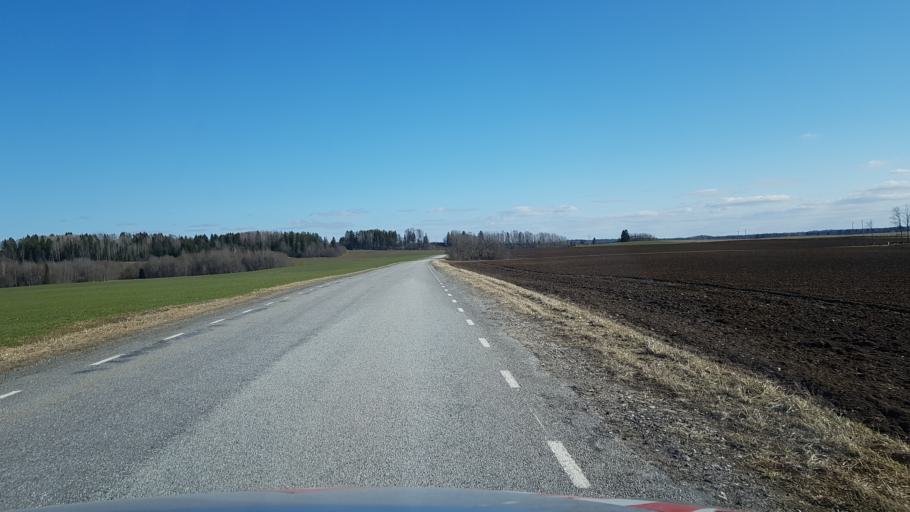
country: EE
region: Laeaene-Virumaa
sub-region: Kadrina vald
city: Kadrina
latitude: 59.3579
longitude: 26.0646
